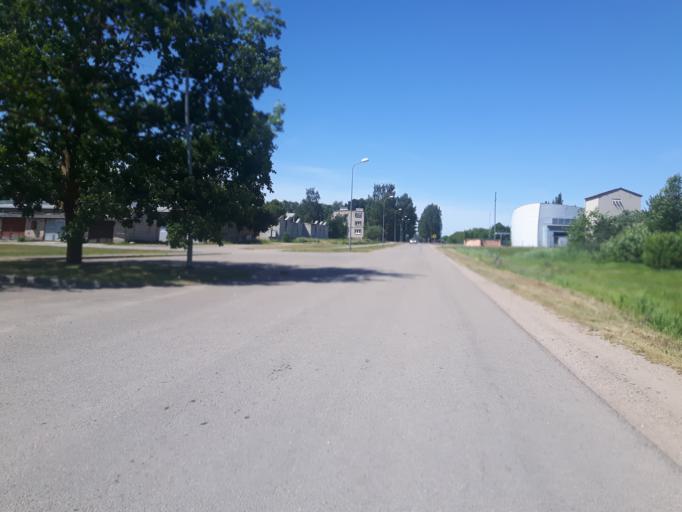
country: LV
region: Grobina
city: Grobina
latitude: 56.5367
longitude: 21.1745
